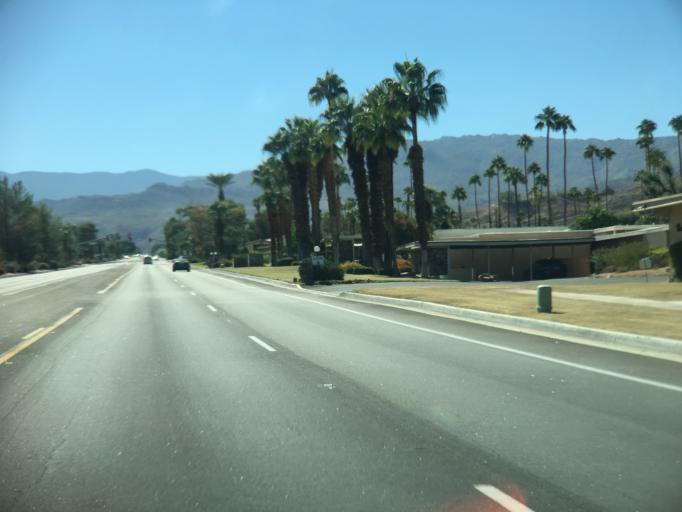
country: US
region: California
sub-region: Riverside County
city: Palm Desert
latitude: 33.7144
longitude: -116.3929
